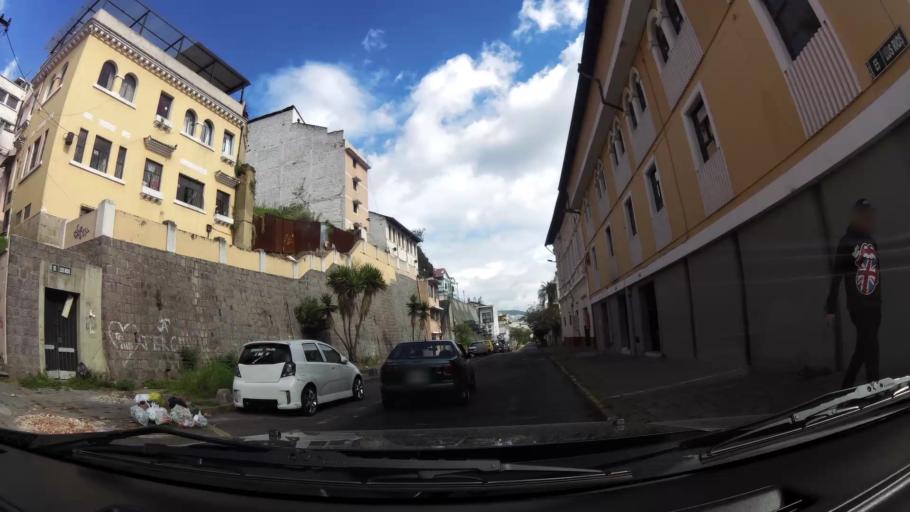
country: EC
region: Pichincha
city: Quito
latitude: -0.2191
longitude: -78.5042
